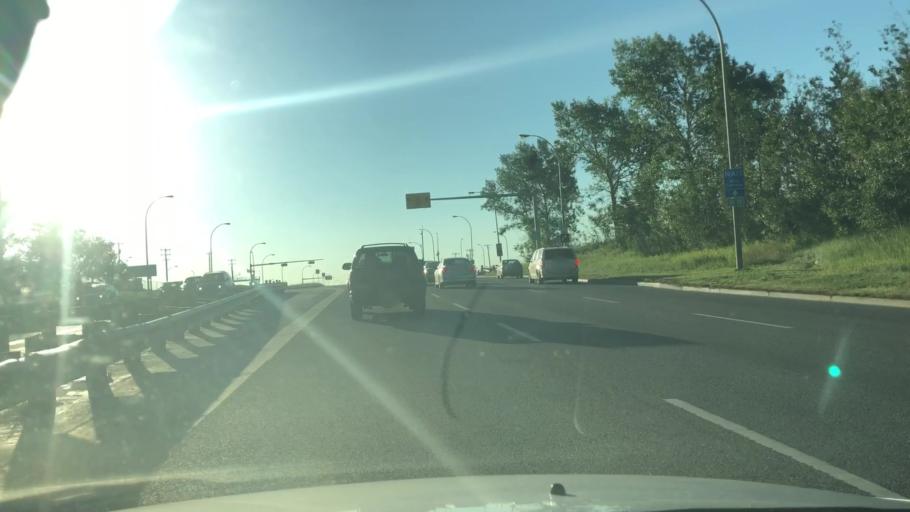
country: CA
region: Alberta
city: Edmonton
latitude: 53.5805
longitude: -113.5290
